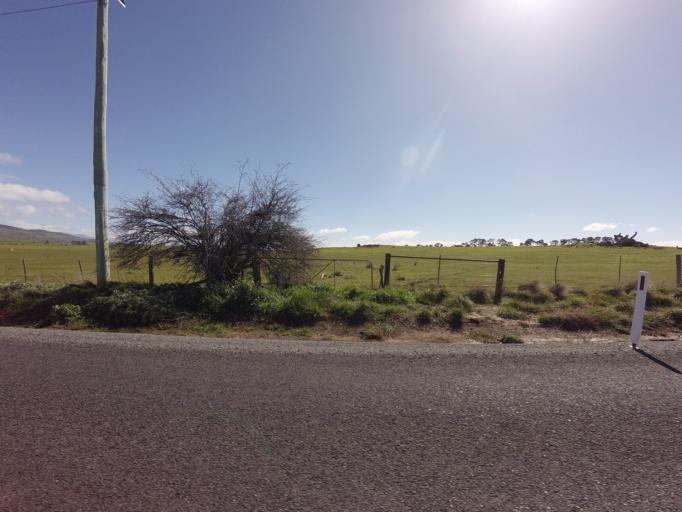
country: AU
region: Tasmania
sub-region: Northern Midlands
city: Evandale
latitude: -41.9096
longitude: 147.3834
